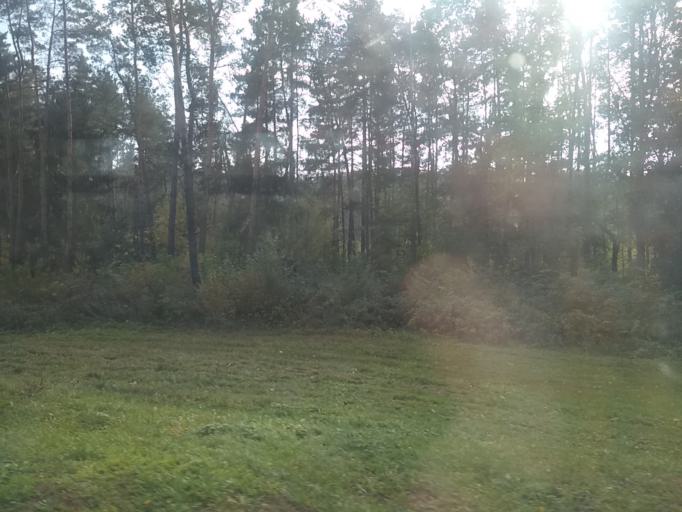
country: BY
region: Minsk
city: Machulishchy
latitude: 53.7844
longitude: 27.6065
